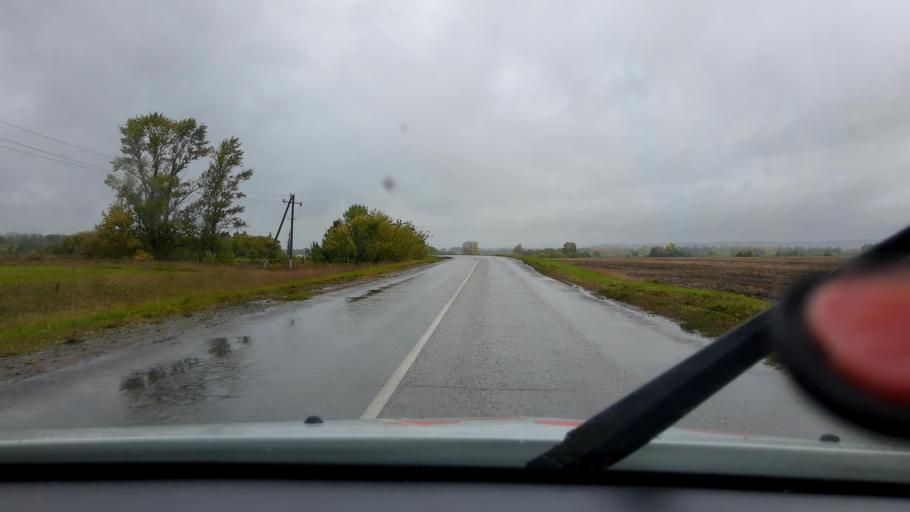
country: RU
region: Bashkortostan
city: Ulukulevo
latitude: 54.4077
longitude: 56.3747
